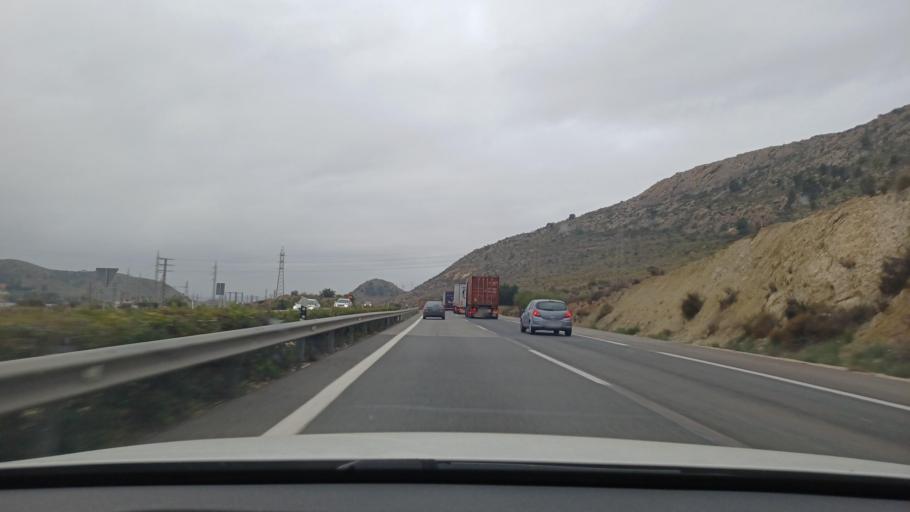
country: ES
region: Valencia
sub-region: Provincia de Alicante
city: Elda
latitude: 38.4427
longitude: -0.7826
